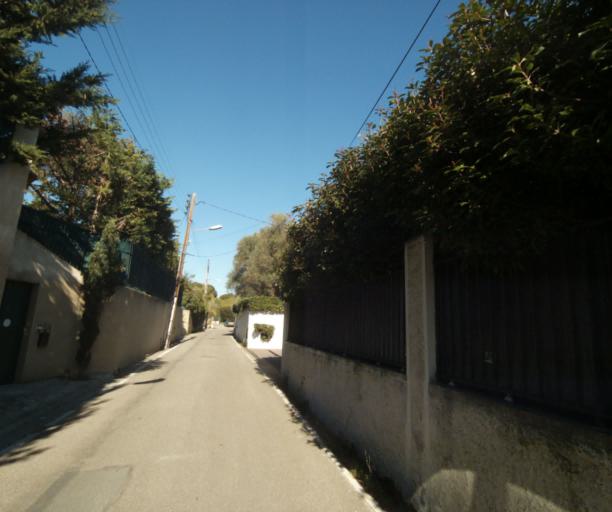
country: FR
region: Provence-Alpes-Cote d'Azur
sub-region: Departement des Alpes-Maritimes
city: Antibes
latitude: 43.5578
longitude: 7.1244
